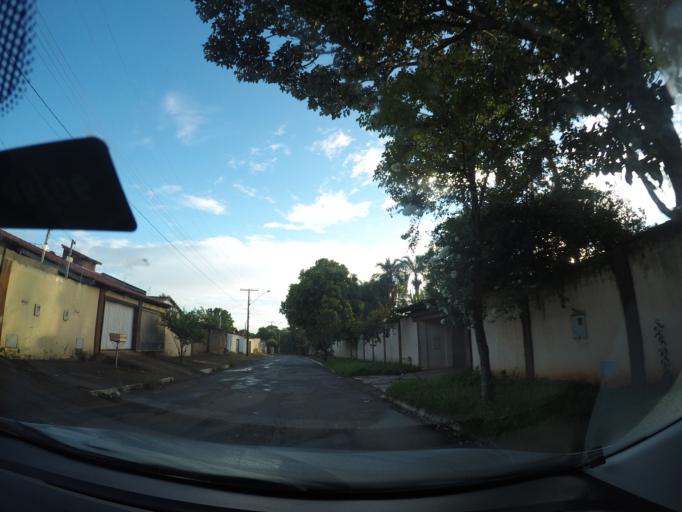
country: BR
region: Goias
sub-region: Goiania
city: Goiania
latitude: -16.7014
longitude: -49.3493
